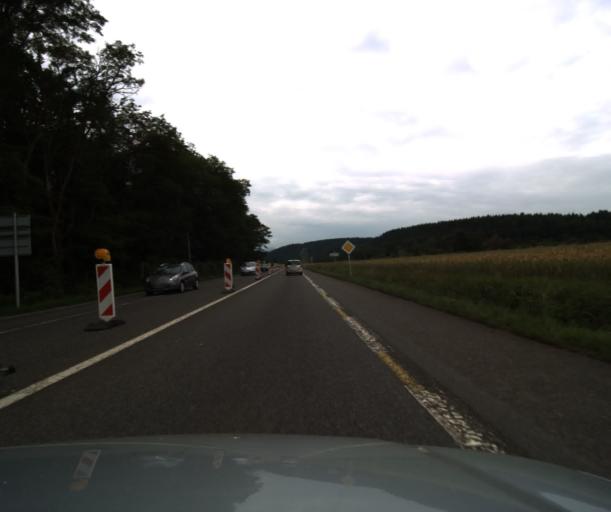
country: FR
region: Midi-Pyrenees
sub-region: Departement des Hautes-Pyrenees
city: Ossun
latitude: 43.1602
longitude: -0.0158
